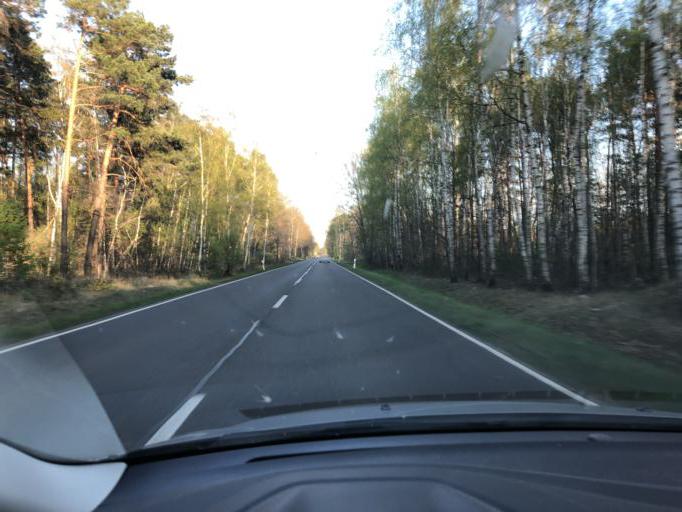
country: DE
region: Brandenburg
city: Welzow
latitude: 51.5457
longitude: 14.1655
